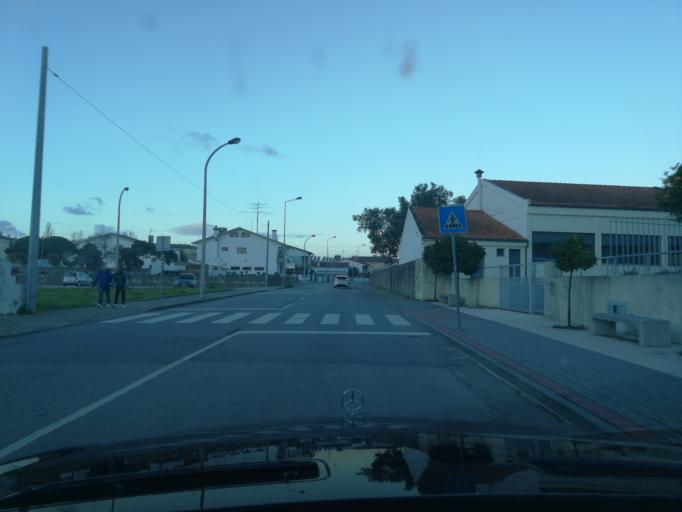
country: PT
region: Aveiro
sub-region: Estarreja
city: Estarreja
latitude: 40.7576
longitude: -8.5743
